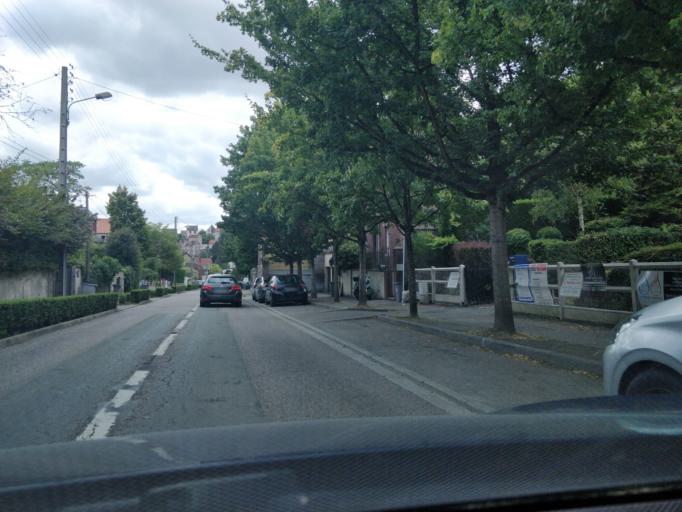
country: FR
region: Haute-Normandie
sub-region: Departement de la Seine-Maritime
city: Mont-Saint-Aignan
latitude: 49.4617
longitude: 1.0952
